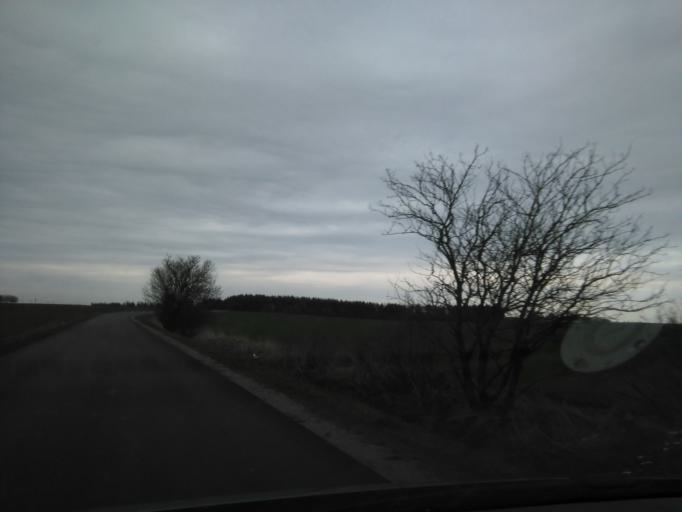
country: DK
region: North Denmark
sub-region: Mariagerfjord Kommune
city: Hobro
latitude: 56.6683
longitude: 9.8139
